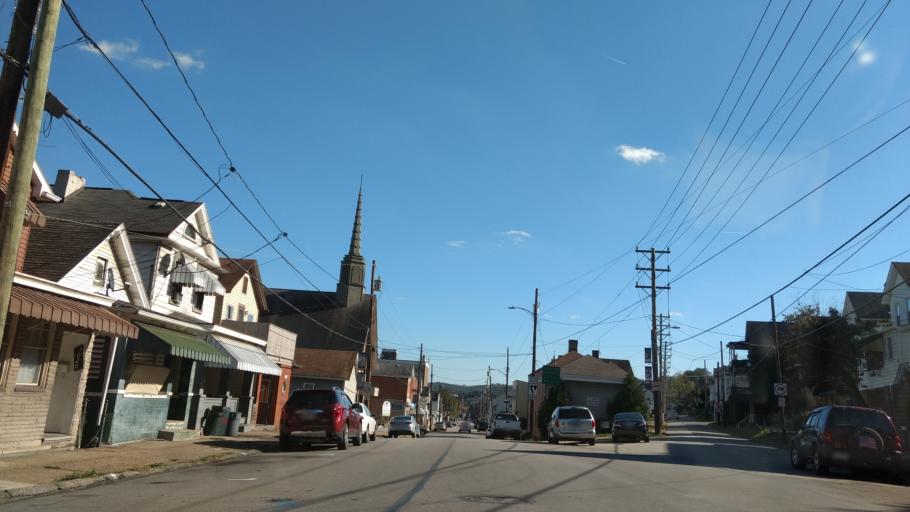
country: US
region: Pennsylvania
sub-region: Washington County
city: North Charleroi
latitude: 40.1438
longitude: -79.9048
